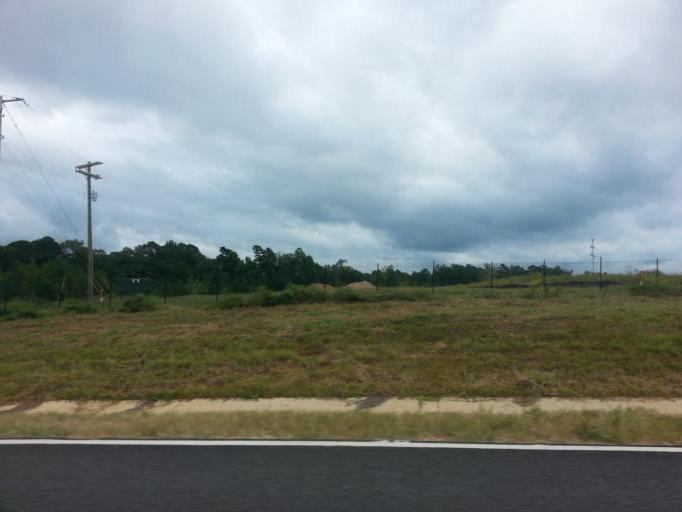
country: US
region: Alabama
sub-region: Conecuh County
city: Evergreen
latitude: 31.4598
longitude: -86.9633
